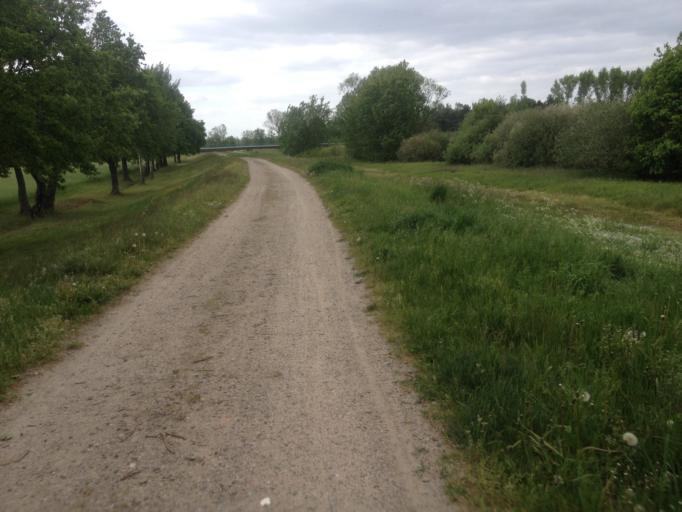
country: DE
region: Brandenburg
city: Drehnow
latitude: 51.8234
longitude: 14.3529
